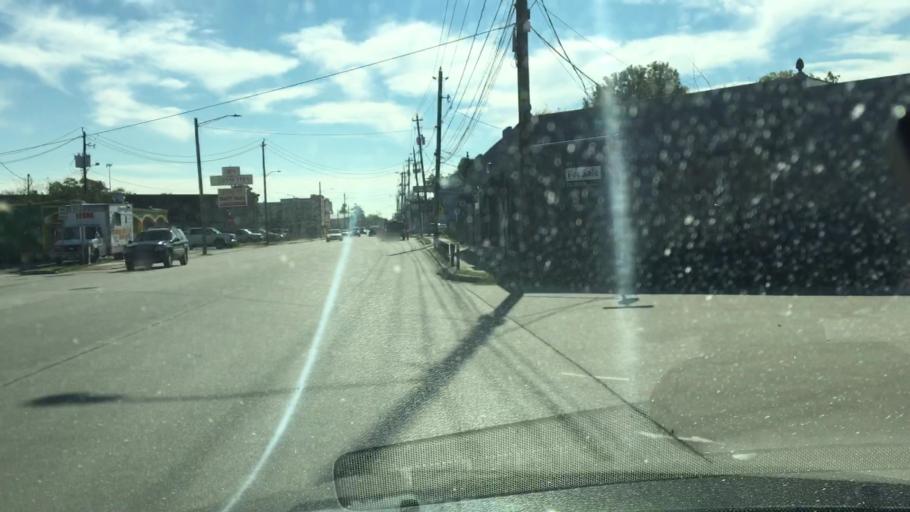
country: US
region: Texas
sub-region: Harris County
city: Houston
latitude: 29.7927
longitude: -95.3756
